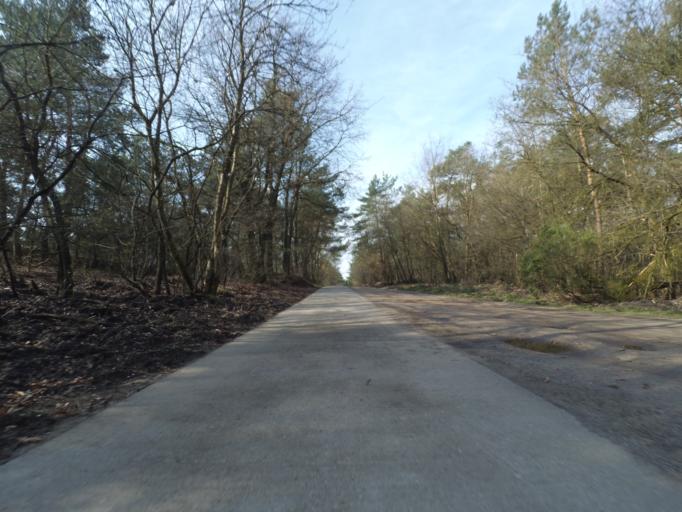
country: NL
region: Gelderland
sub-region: Gemeente Ede
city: Harskamp
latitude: 52.1722
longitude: 5.8376
